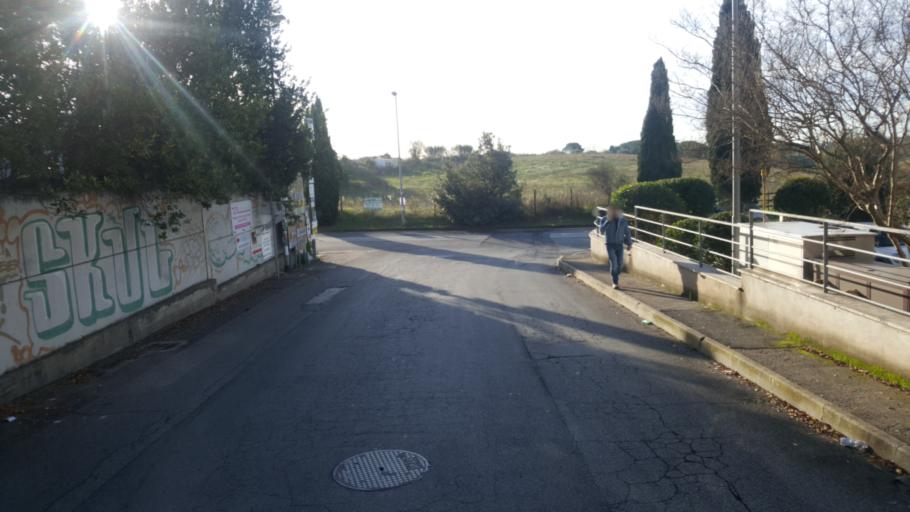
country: IT
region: Latium
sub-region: Citta metropolitana di Roma Capitale
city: Formello
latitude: 42.0497
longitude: 12.4034
